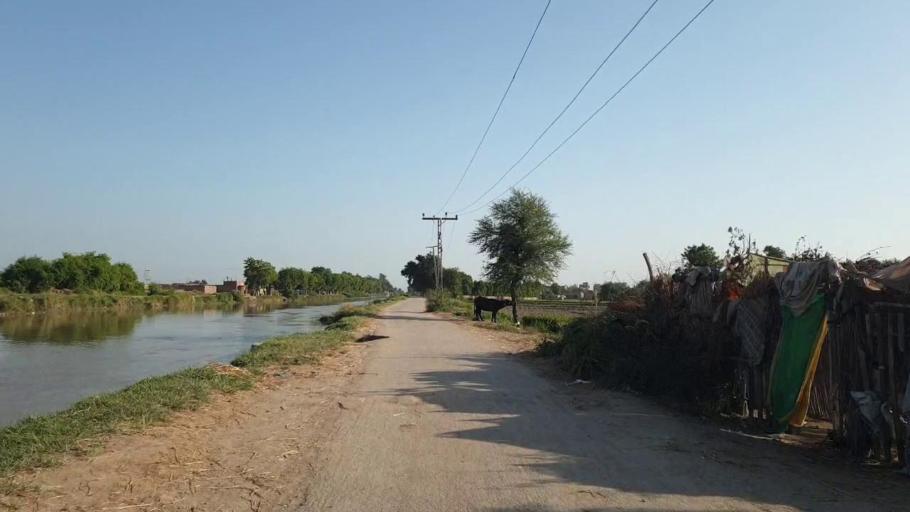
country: PK
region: Sindh
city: Hyderabad
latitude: 25.3220
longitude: 68.4272
